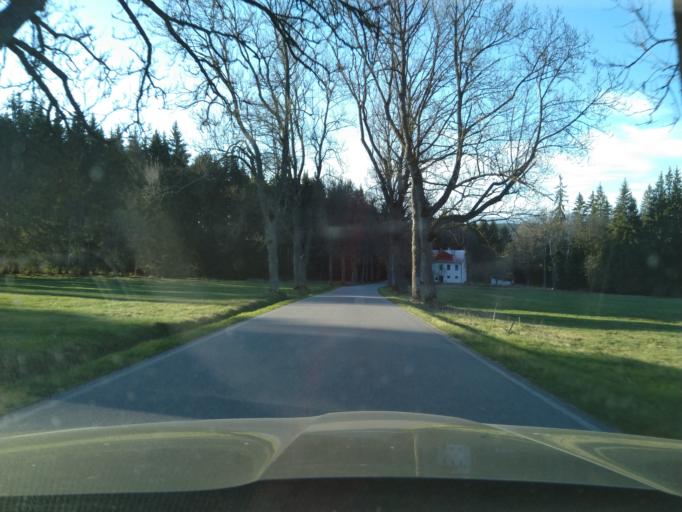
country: DE
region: Bavaria
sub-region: Lower Bavaria
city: Haidmuhle
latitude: 48.8729
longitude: 13.7894
